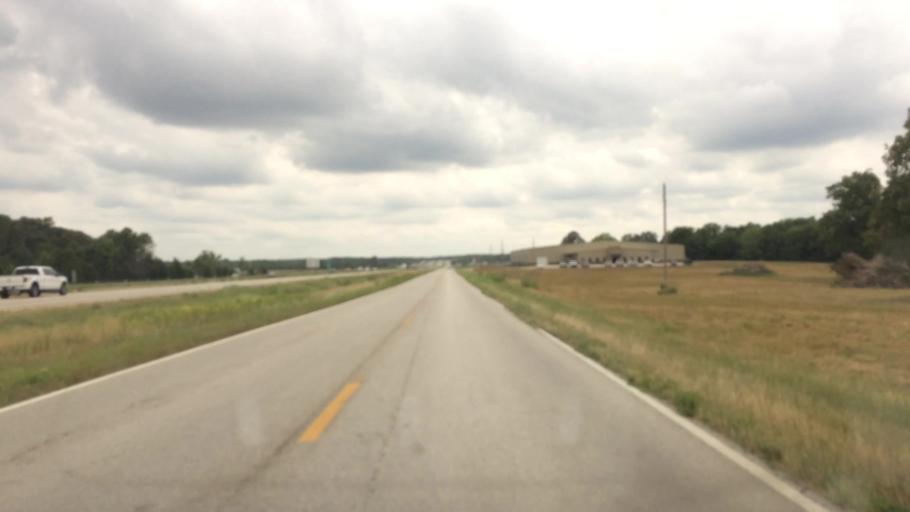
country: US
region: Missouri
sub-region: Greene County
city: Strafford
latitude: 37.2979
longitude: -93.0165
